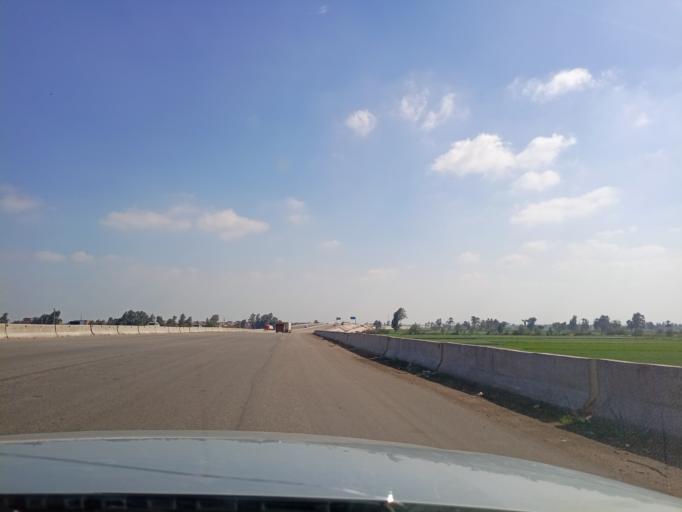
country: EG
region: Eastern Province
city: Mashtul as Suq
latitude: 30.4624
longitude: 31.3740
